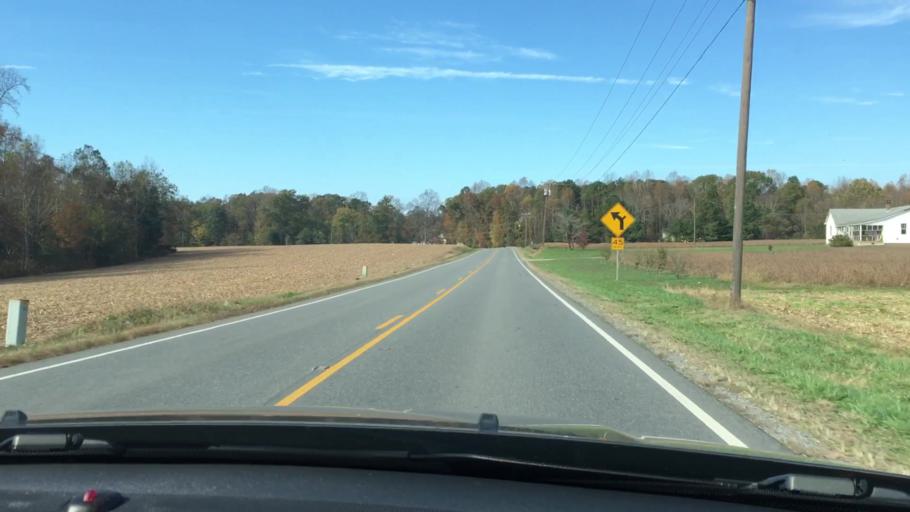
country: US
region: Virginia
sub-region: King William County
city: West Point
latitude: 37.5885
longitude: -76.8561
